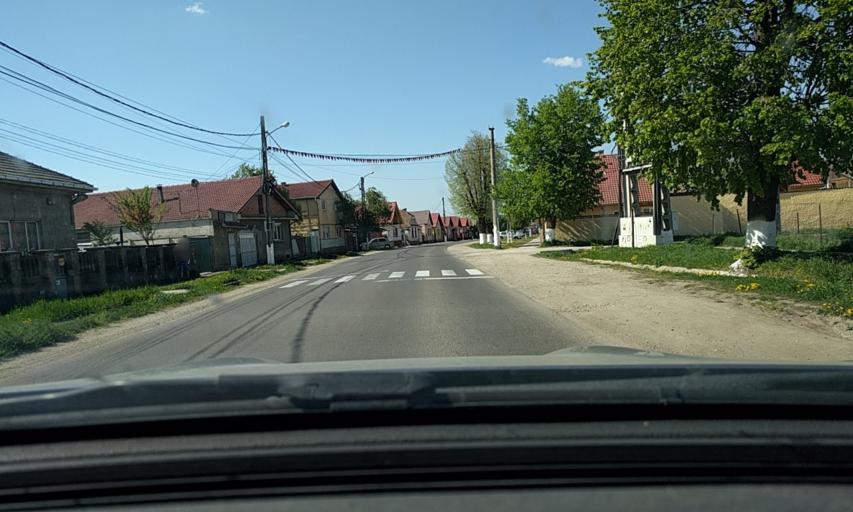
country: RO
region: Brasov
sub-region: Comuna Harman
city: Harman
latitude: 45.7092
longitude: 25.6858
